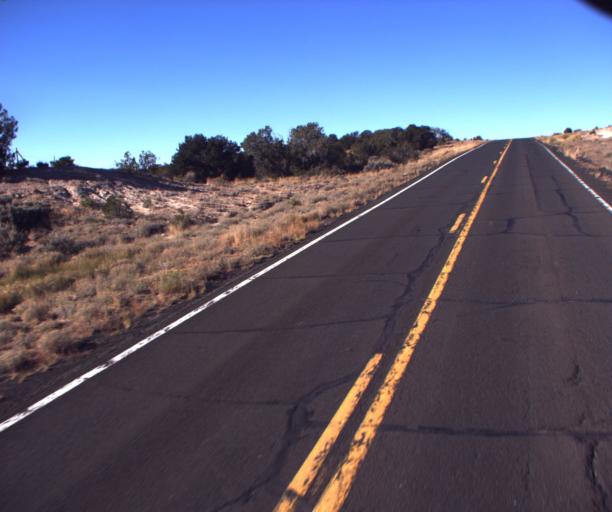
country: US
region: Arizona
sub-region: Navajo County
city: First Mesa
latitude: 35.7651
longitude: -109.9938
